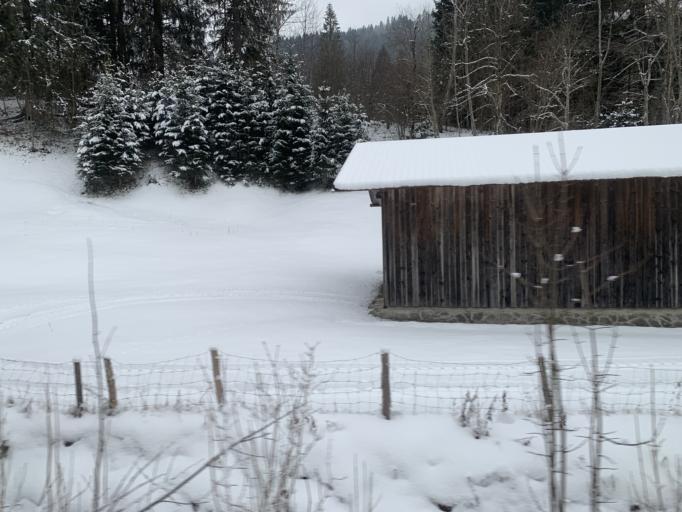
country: DE
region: Bavaria
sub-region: Upper Bavaria
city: Mittenwald
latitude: 47.4875
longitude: 11.1891
